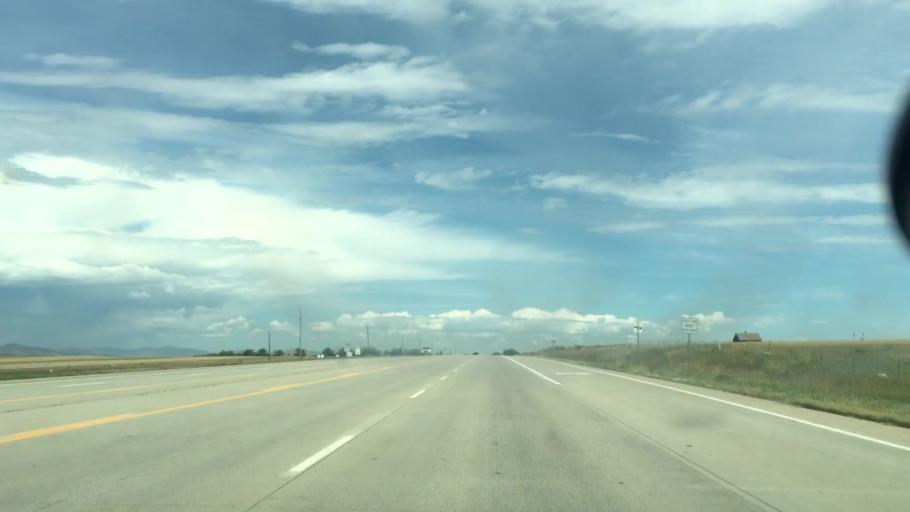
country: US
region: Colorado
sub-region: Boulder County
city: Longmont
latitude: 40.2158
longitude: -105.1023
